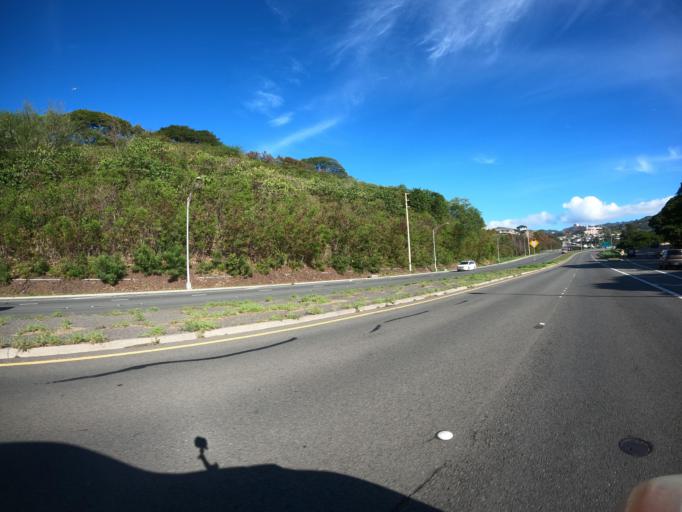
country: US
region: Hawaii
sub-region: Honolulu County
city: Halawa Heights
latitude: 21.3467
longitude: -157.8979
